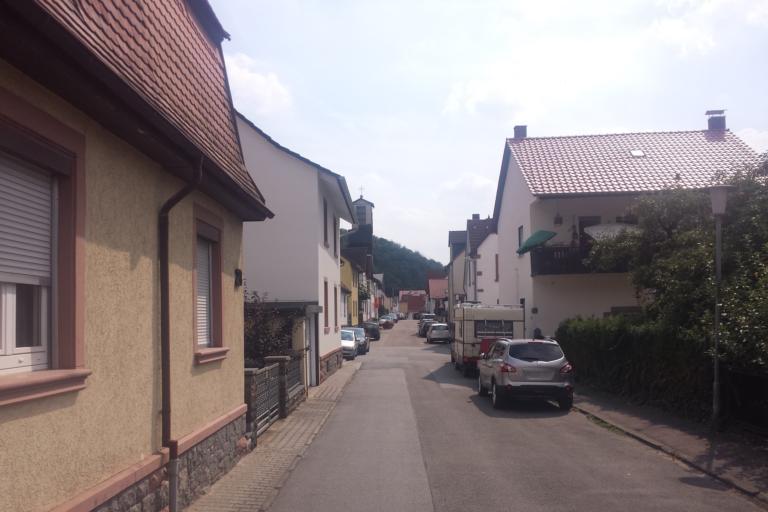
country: DE
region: Baden-Wuerttemberg
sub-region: Karlsruhe Region
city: Hemsbach
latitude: 49.5801
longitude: 8.6604
